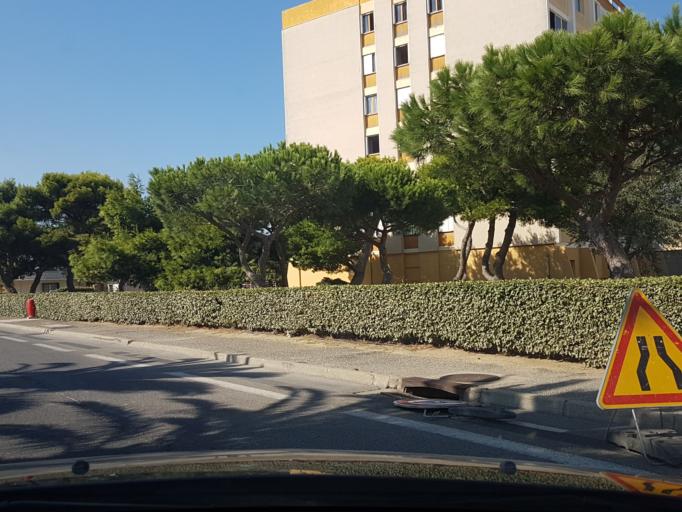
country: FR
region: Languedoc-Roussillon
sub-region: Departement de l'Aude
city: Port-la-Nouvelle
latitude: 43.0183
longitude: 3.0488
